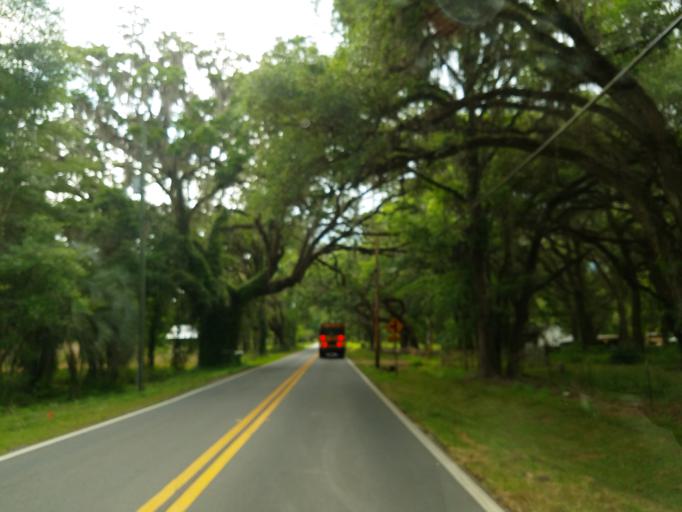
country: US
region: Florida
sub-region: Hernando County
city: Brooksville
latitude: 28.5560
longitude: -82.3657
